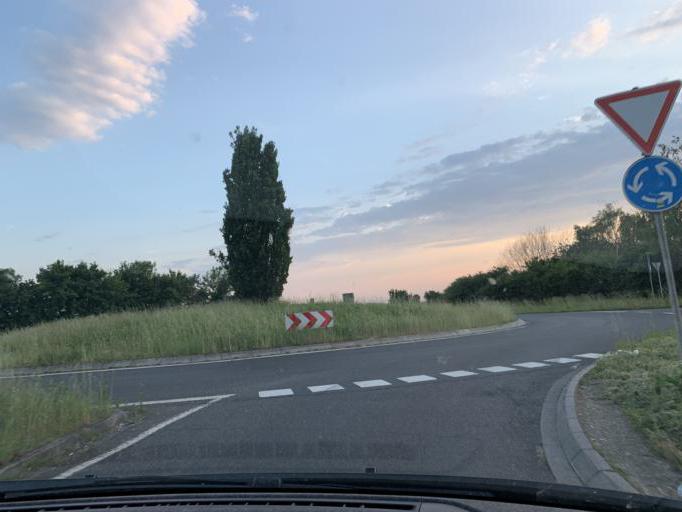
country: DE
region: North Rhine-Westphalia
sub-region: Regierungsbezirk Koln
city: Sinnersdorf
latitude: 51.0238
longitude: 6.8056
